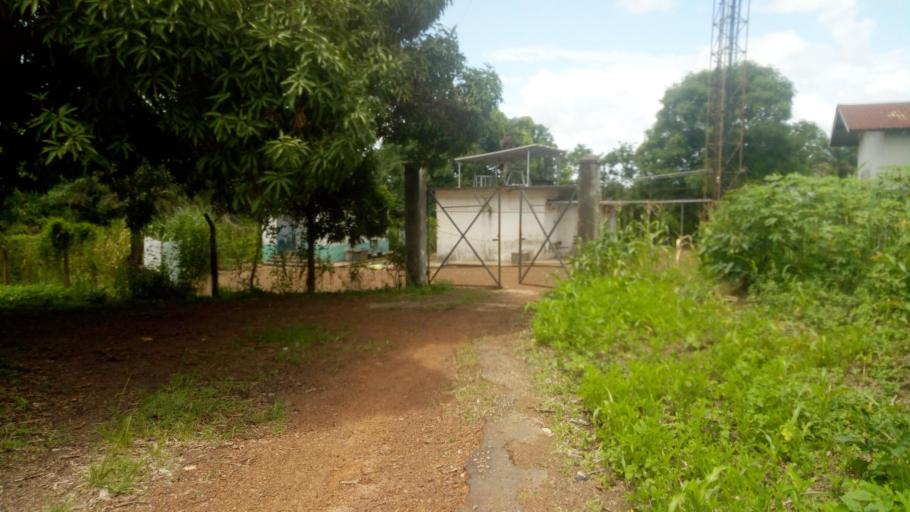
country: SL
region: Northern Province
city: Magburaka
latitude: 8.7172
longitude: -11.9473
